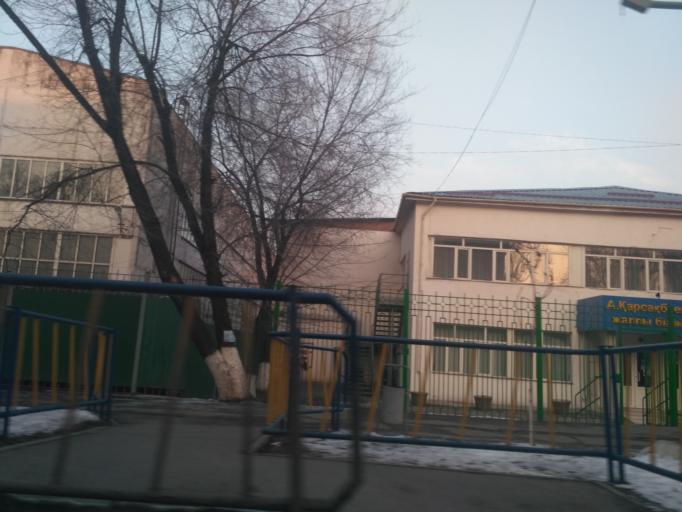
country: KZ
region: Almaty Qalasy
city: Almaty
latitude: 43.2668
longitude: 76.8632
